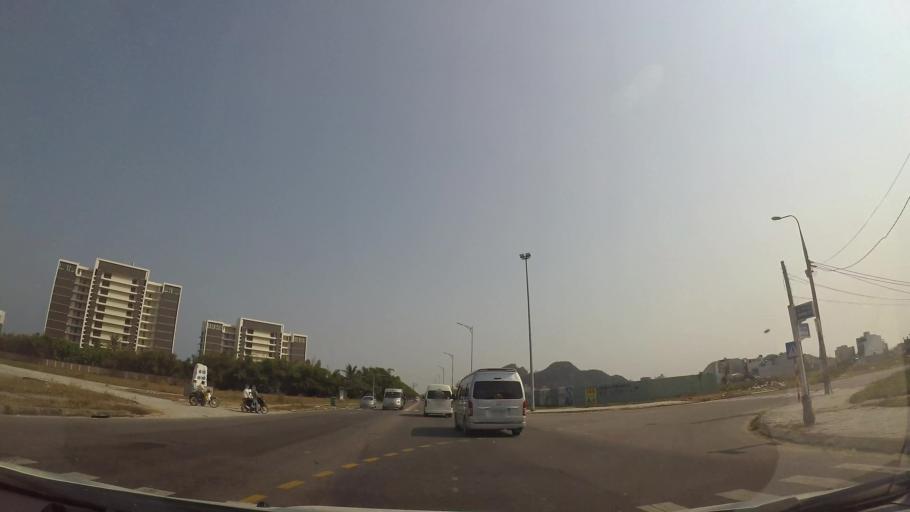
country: VN
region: Da Nang
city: Ngu Hanh Son
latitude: 16.0155
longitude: 108.2609
